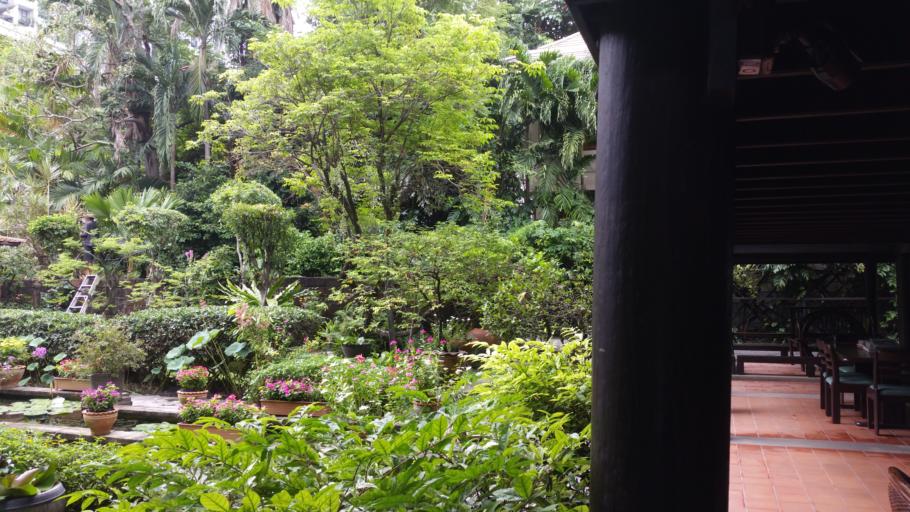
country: TH
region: Bangkok
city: Sathon
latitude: 13.7201
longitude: 100.5337
